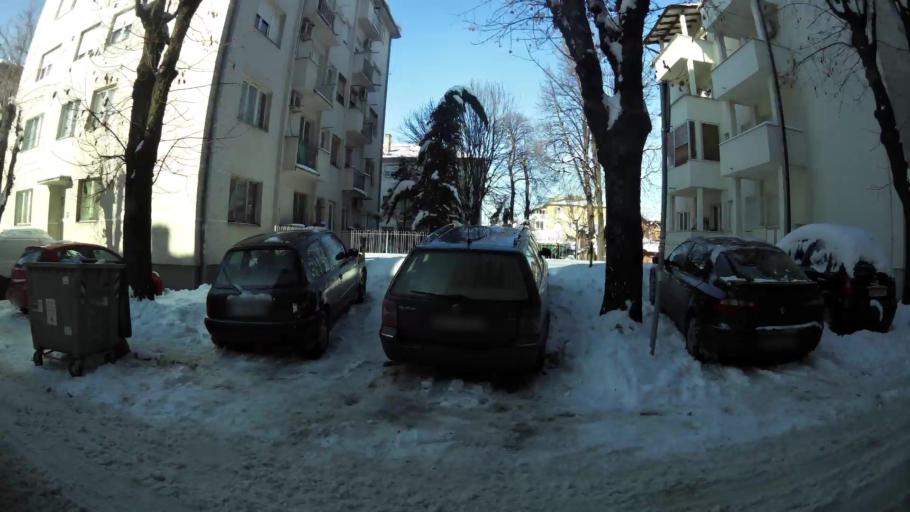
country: RS
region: Central Serbia
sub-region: Belgrade
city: Palilula
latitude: 44.8148
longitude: 20.5152
